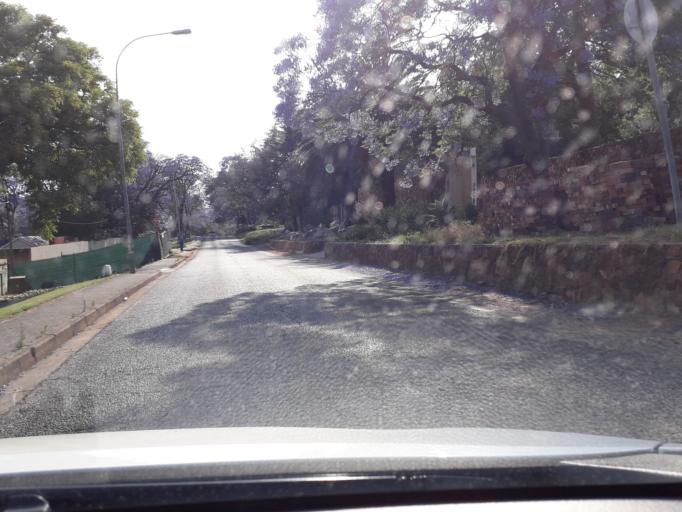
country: ZA
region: Gauteng
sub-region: City of Johannesburg Metropolitan Municipality
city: Roodepoort
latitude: -26.1408
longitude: 27.9647
